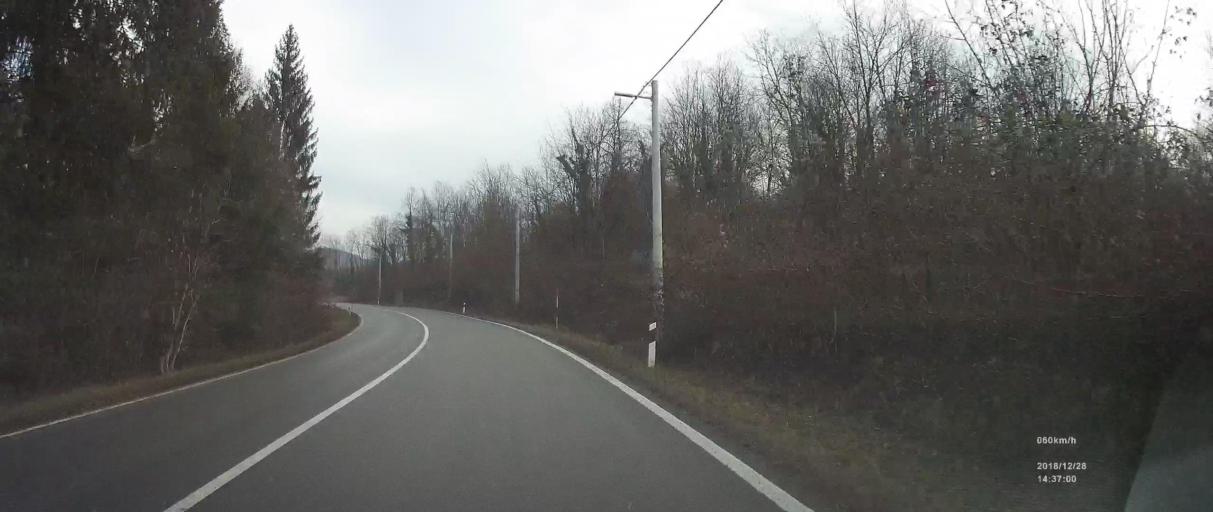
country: HR
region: Primorsko-Goranska
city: Vrbovsko
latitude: 45.4208
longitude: 15.2040
